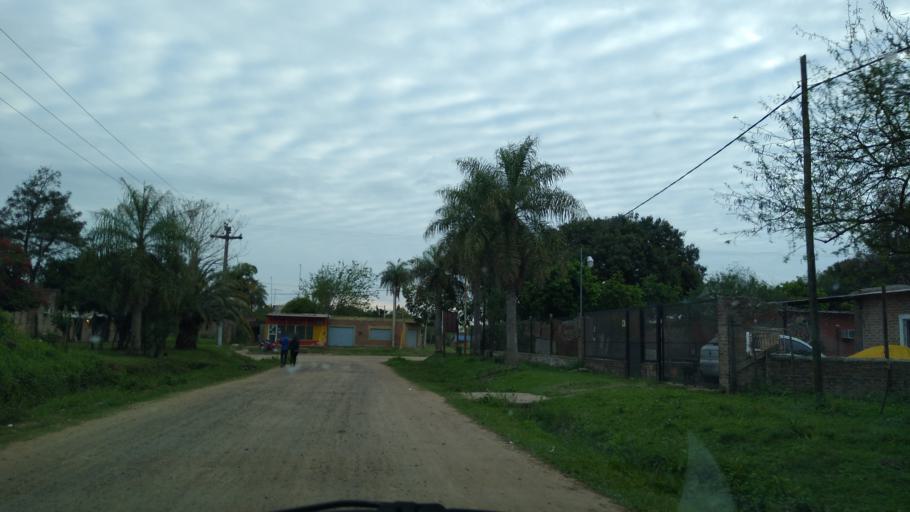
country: AR
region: Chaco
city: Fontana
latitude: -27.4022
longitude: -59.0407
